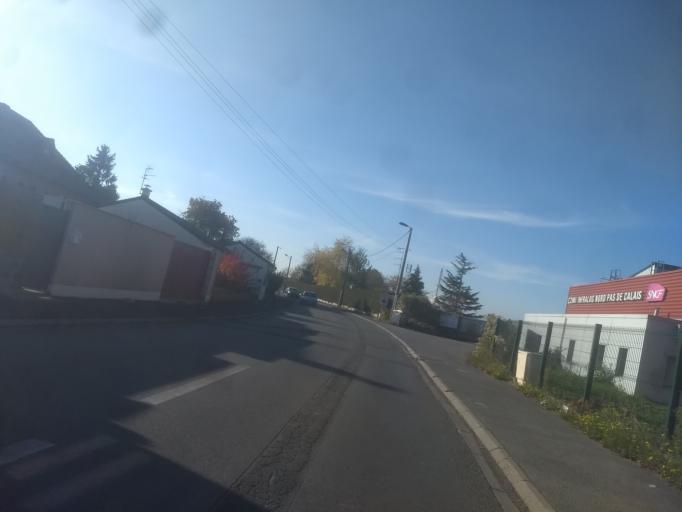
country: FR
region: Nord-Pas-de-Calais
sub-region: Departement du Pas-de-Calais
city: Arras
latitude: 50.2807
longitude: 2.7729
